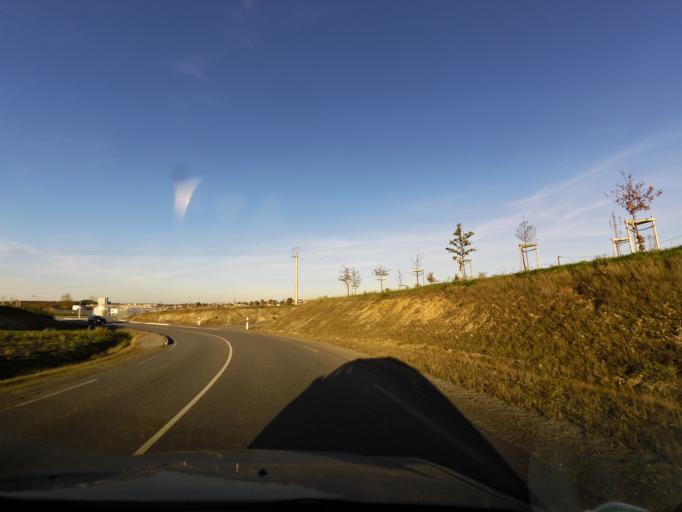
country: FR
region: Brittany
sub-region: Departement d'Ille-et-Vilaine
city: Crevin
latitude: 47.9296
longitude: -1.6703
